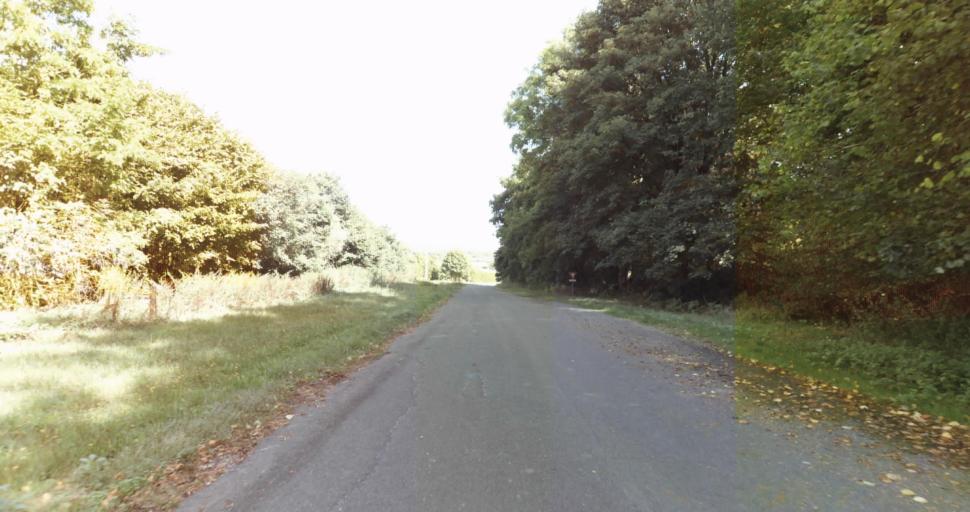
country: FR
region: Lower Normandy
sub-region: Departement de l'Orne
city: Sees
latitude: 48.7125
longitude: 0.1944
